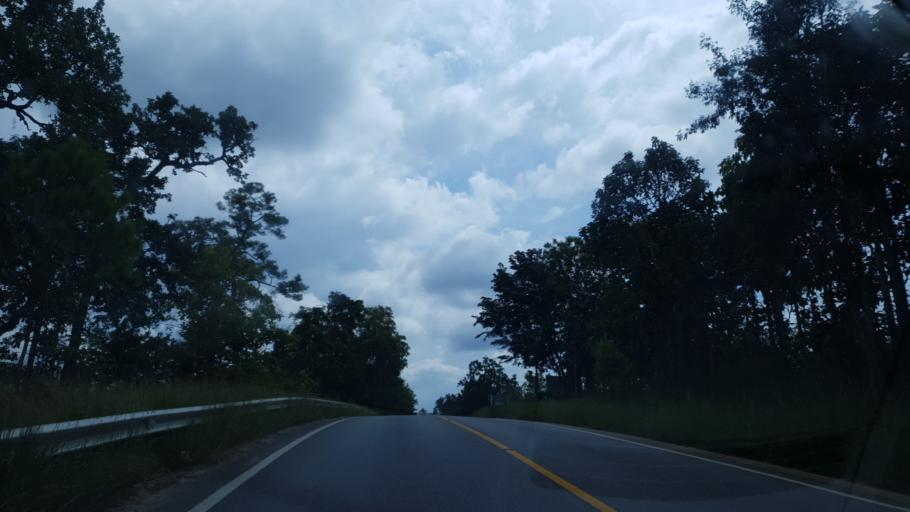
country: TH
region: Mae Hong Son
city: Khun Yuam
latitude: 18.8026
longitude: 97.9308
